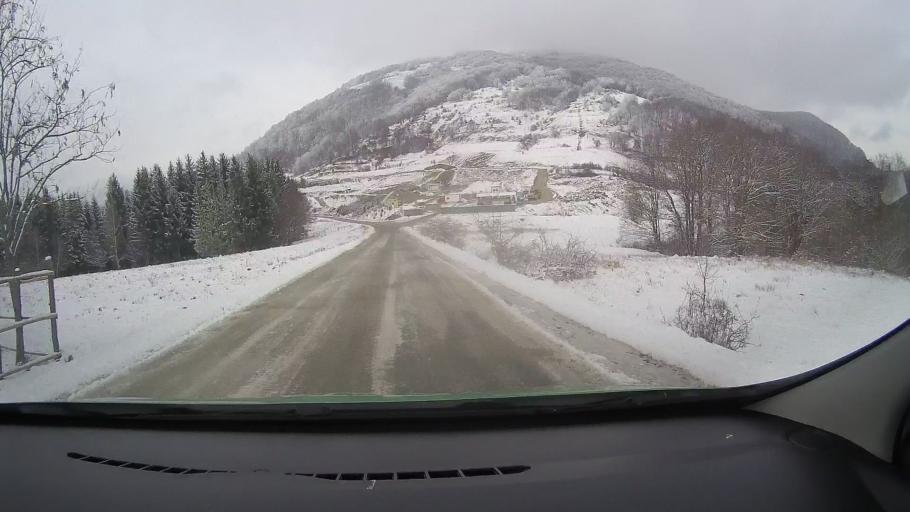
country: RO
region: Alba
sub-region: Comuna Almasu Mare
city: Almasu Mare
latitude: 46.0973
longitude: 23.1589
